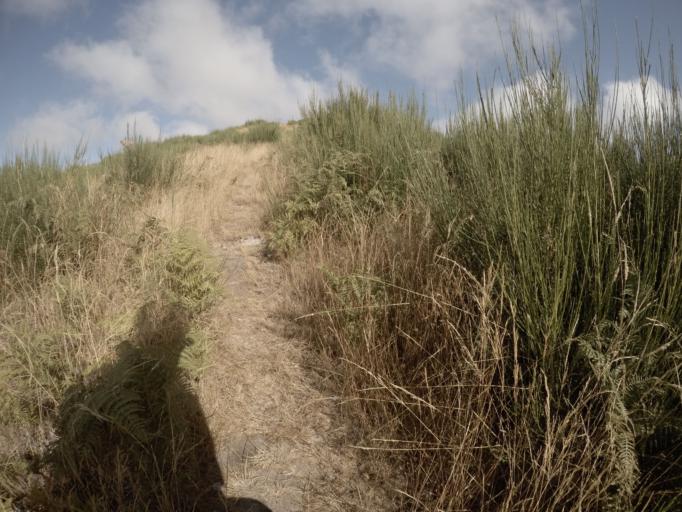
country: PT
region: Madeira
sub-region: Camara de Lobos
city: Curral das Freiras
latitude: 32.7102
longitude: -16.9879
